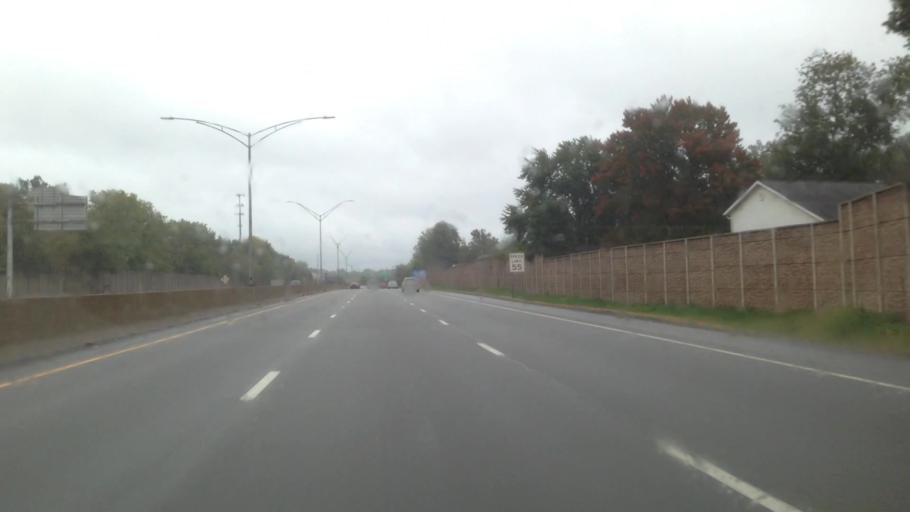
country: US
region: Ohio
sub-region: Summit County
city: Silver Lake
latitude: 41.1552
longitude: -81.4700
